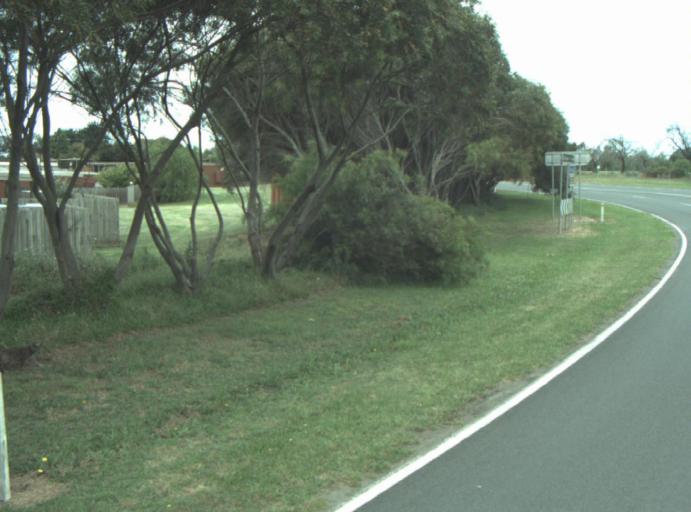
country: AU
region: Victoria
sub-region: Greater Geelong
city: Clifton Springs
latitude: -38.1205
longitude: 144.6559
